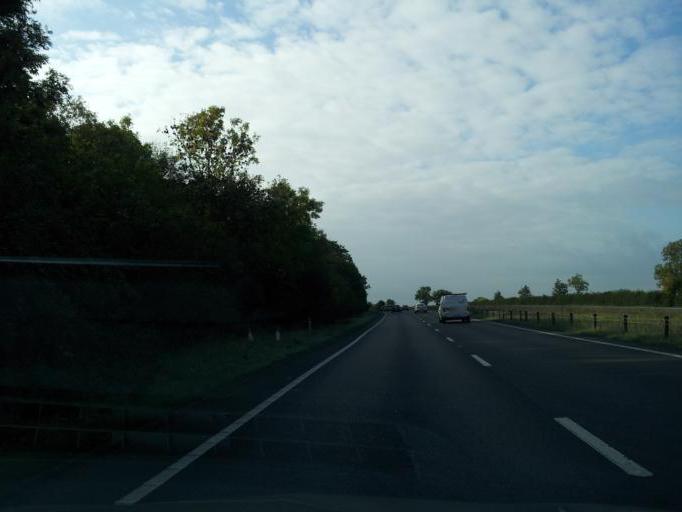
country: GB
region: England
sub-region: Northamptonshire
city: Silverstone
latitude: 52.0754
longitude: -1.0504
